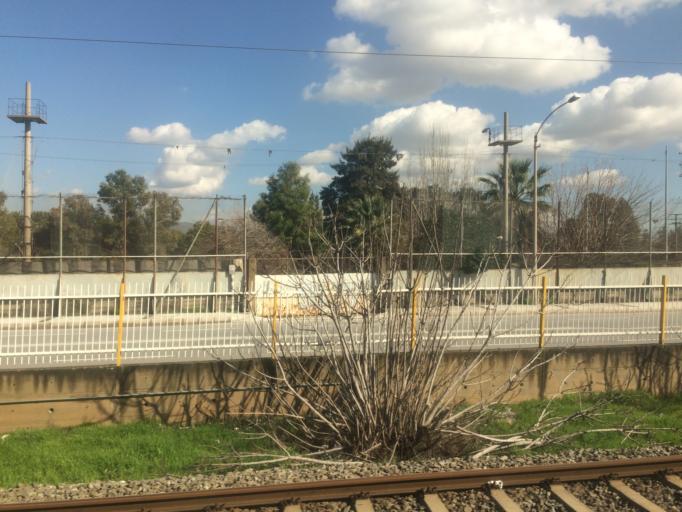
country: TR
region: Izmir
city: Izmir
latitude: 38.4575
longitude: 27.1686
